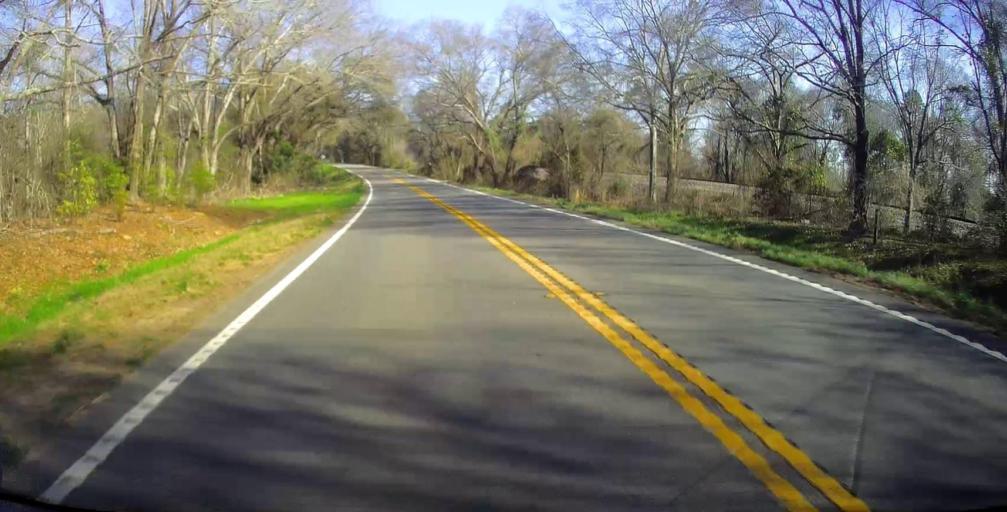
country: US
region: Georgia
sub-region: Macon County
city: Oglethorpe
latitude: 32.3375
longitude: -84.1275
